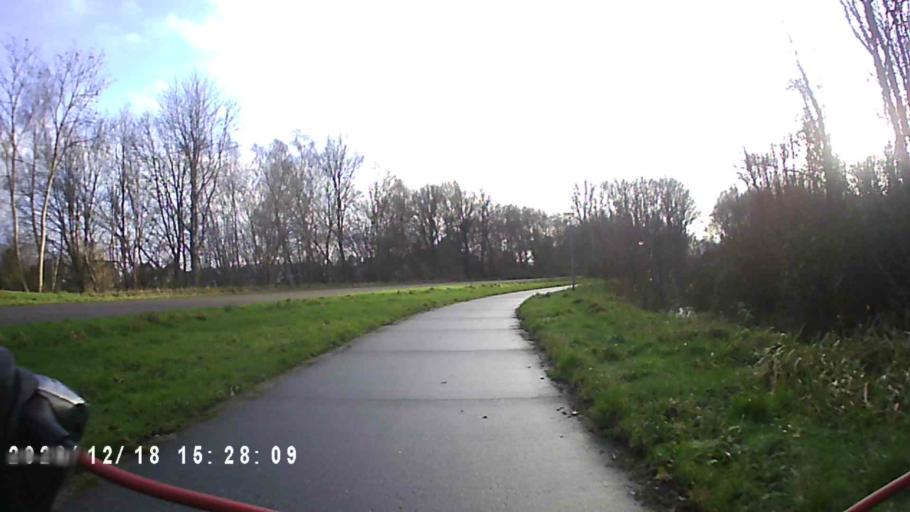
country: NL
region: Groningen
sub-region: Gemeente Hoogezand-Sappemeer
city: Hoogezand
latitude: 53.1472
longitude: 6.7072
